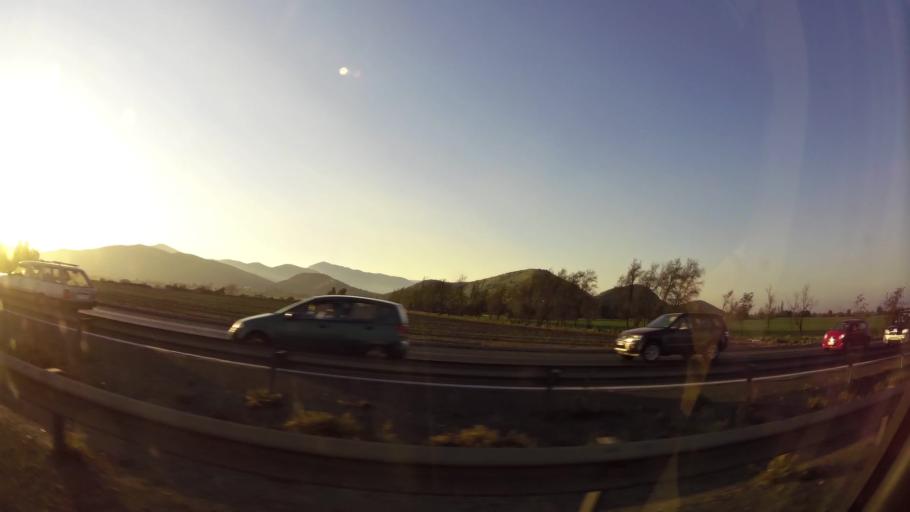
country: CL
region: Santiago Metropolitan
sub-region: Provincia de Talagante
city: Penaflor
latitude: -33.5530
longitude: -70.8140
